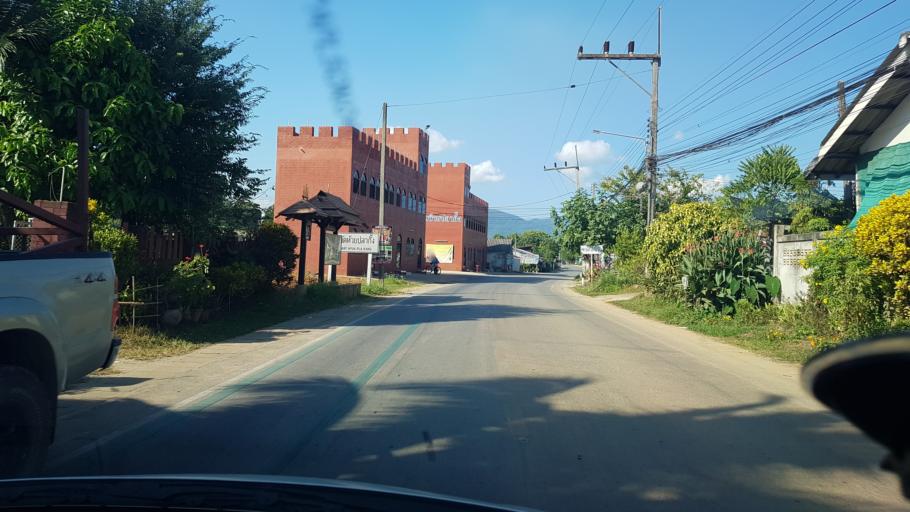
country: TH
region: Chiang Rai
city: Chiang Rai
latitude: 19.9493
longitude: 99.8097
